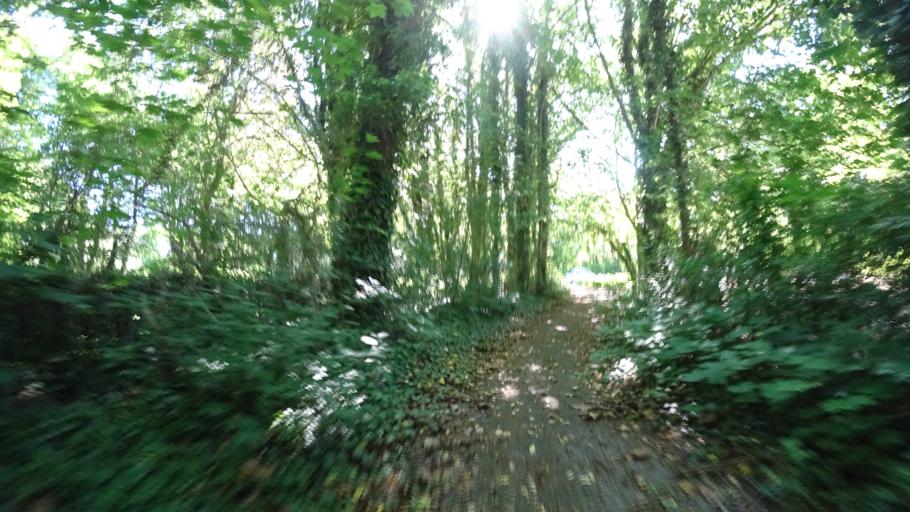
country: DE
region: North Rhine-Westphalia
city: Erwitte
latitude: 51.6321
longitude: 8.3504
